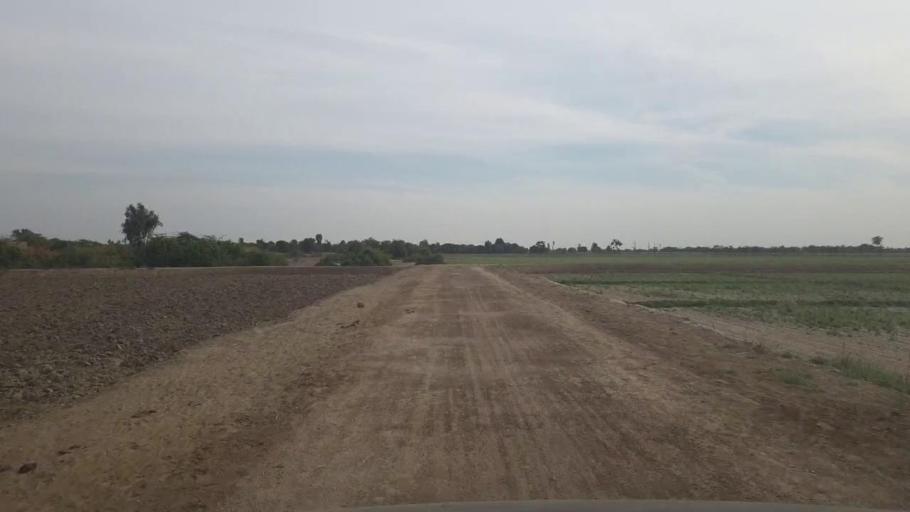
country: PK
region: Sindh
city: Kunri
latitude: 25.2793
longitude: 69.6001
